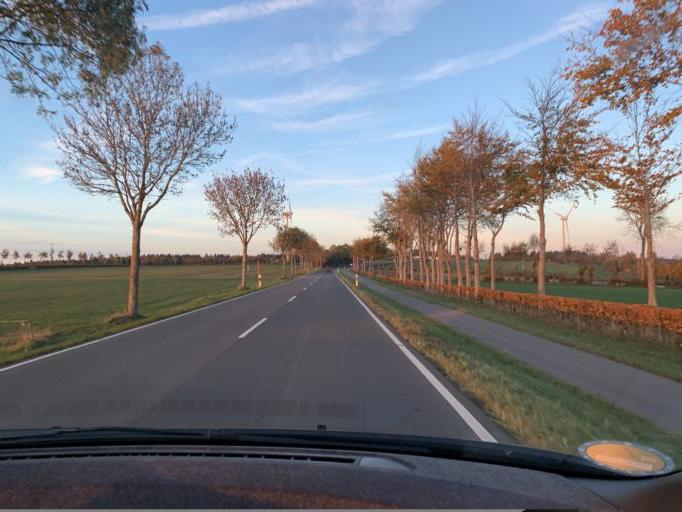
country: DE
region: North Rhine-Westphalia
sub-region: Regierungsbezirk Koln
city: Simmerath
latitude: 50.6382
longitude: 6.3443
